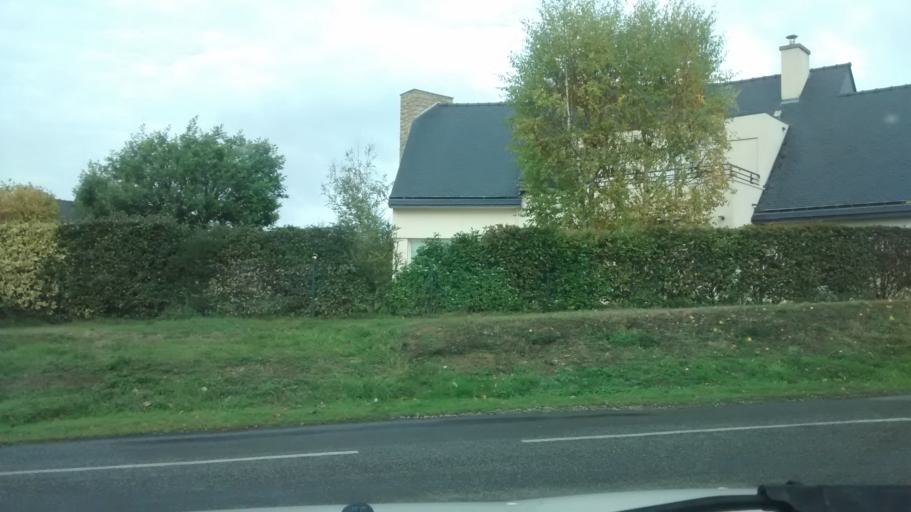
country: FR
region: Brittany
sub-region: Departement d'Ille-et-Vilaine
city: Chateaubourg
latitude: 48.1168
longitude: -1.3968
